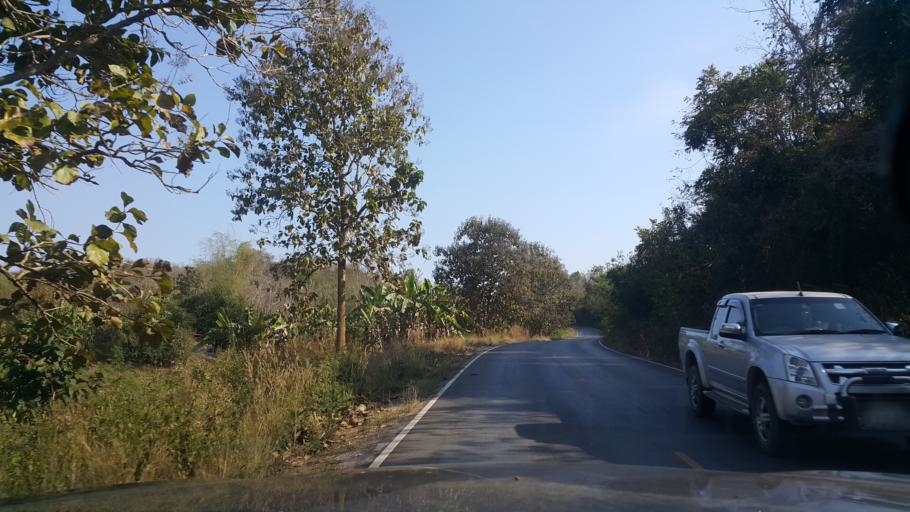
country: TH
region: Loei
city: Chiang Khan
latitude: 17.8404
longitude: 101.6338
